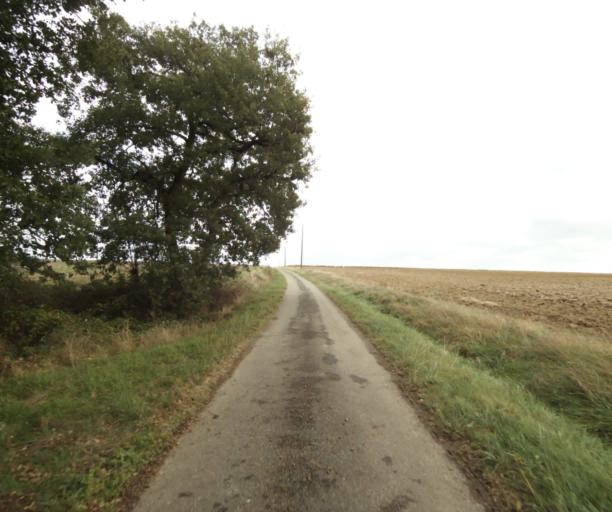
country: FR
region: Midi-Pyrenees
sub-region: Departement du Tarn-et-Garonne
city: Beaumont-de-Lomagne
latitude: 43.8881
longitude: 1.0847
